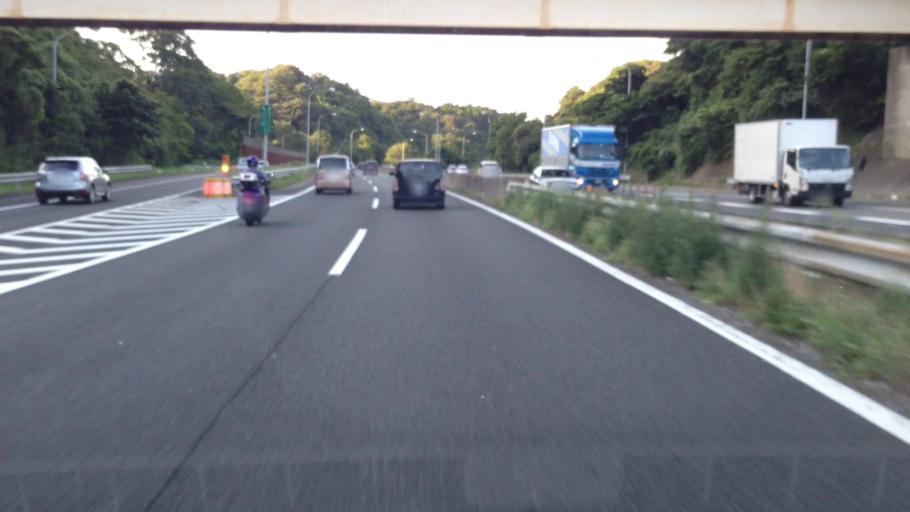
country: JP
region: Kanagawa
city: Zushi
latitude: 35.3467
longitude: 139.5930
